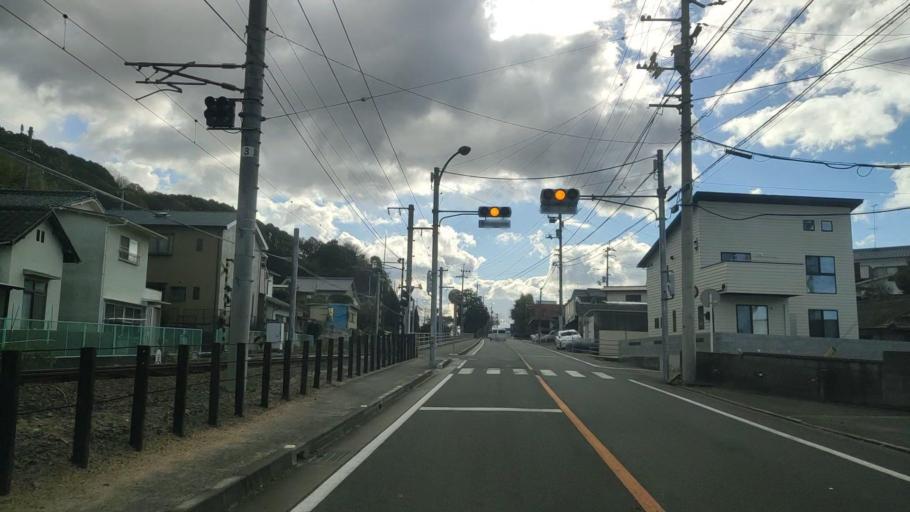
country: JP
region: Ehime
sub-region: Shikoku-chuo Shi
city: Matsuyama
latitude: 33.8800
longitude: 132.7025
